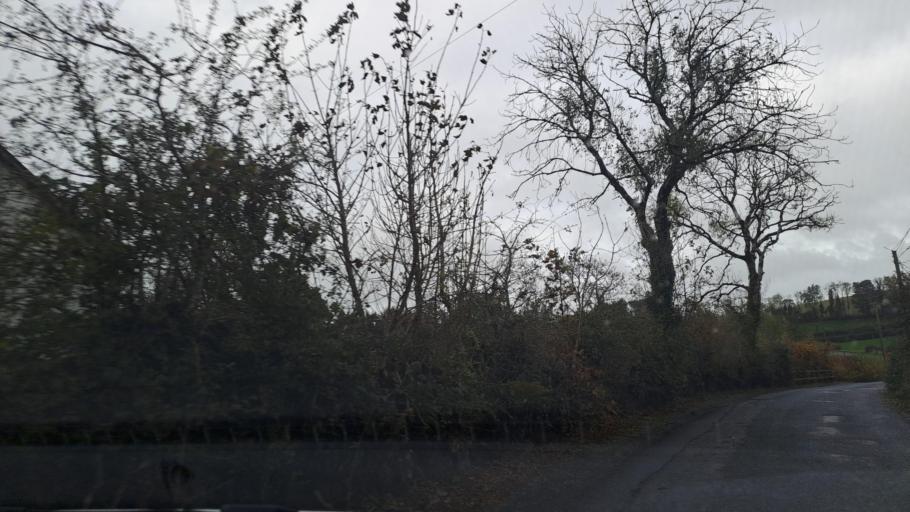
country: IE
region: Ulster
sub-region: An Cabhan
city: Kingscourt
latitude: 53.9669
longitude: -6.8684
